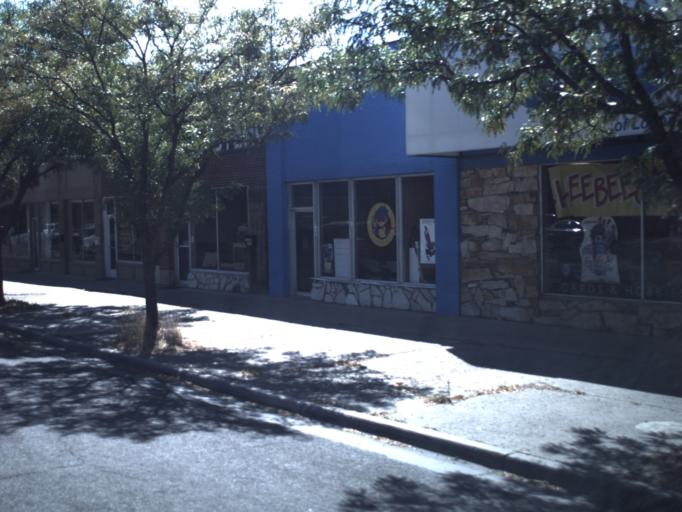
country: US
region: Utah
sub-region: Cache County
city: Logan
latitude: 41.7417
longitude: -111.8348
